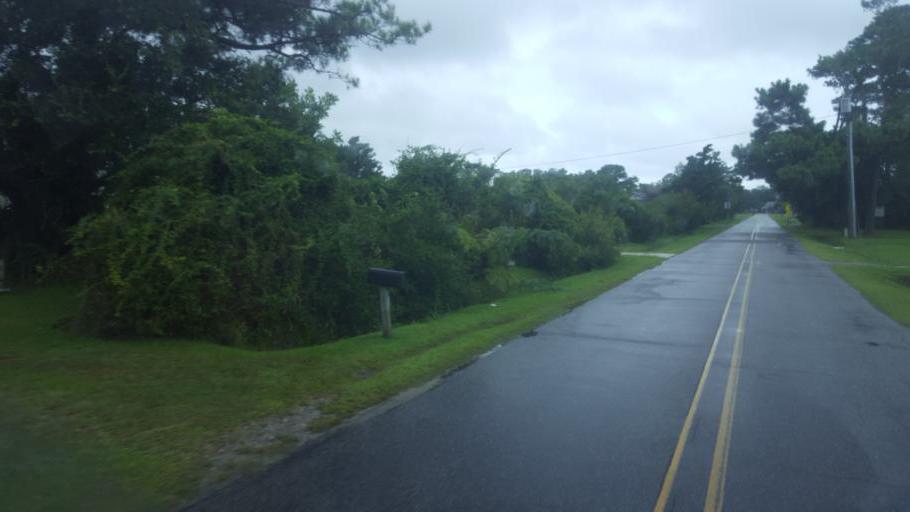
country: US
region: North Carolina
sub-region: Dare County
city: Wanchese
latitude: 35.8404
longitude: -75.6242
